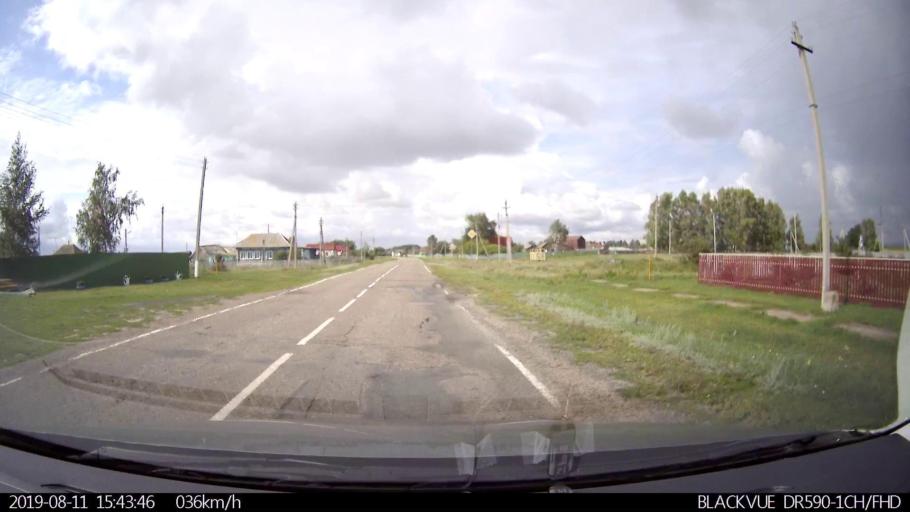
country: RU
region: Ulyanovsk
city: Ignatovka
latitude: 53.8782
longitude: 47.6586
